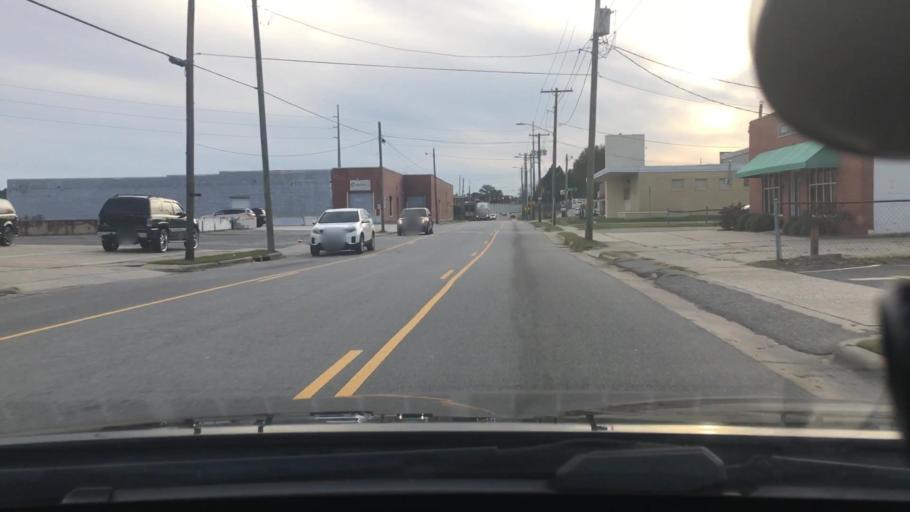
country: US
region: North Carolina
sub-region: Pitt County
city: Greenville
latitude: 35.6026
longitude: -77.3888
